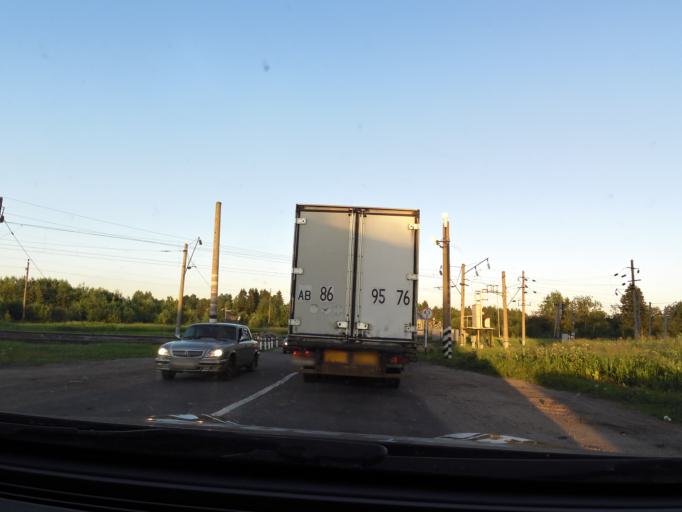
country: RU
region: Jaroslavl
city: Prechistoye
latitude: 58.4108
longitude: 40.3599
